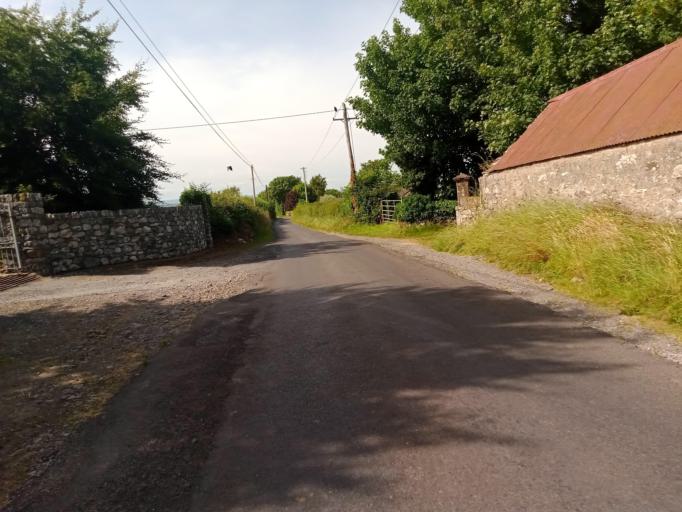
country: IE
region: Leinster
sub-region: Laois
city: Rathdowney
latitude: 52.8116
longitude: -7.4697
